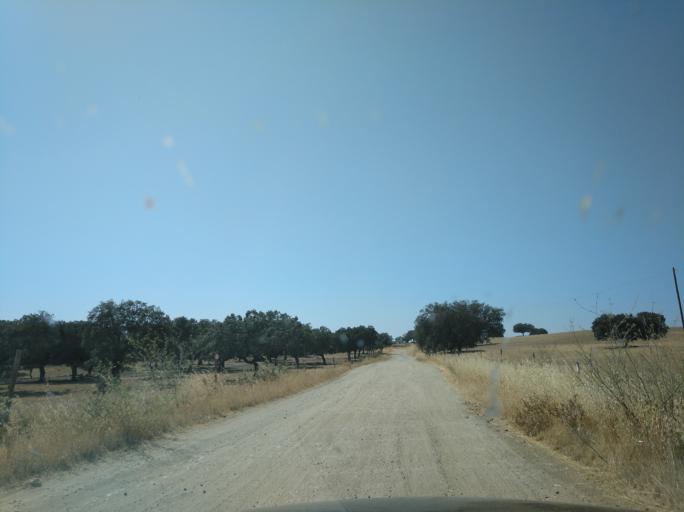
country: PT
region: Portalegre
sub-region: Campo Maior
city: Campo Maior
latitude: 39.0258
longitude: -6.9773
